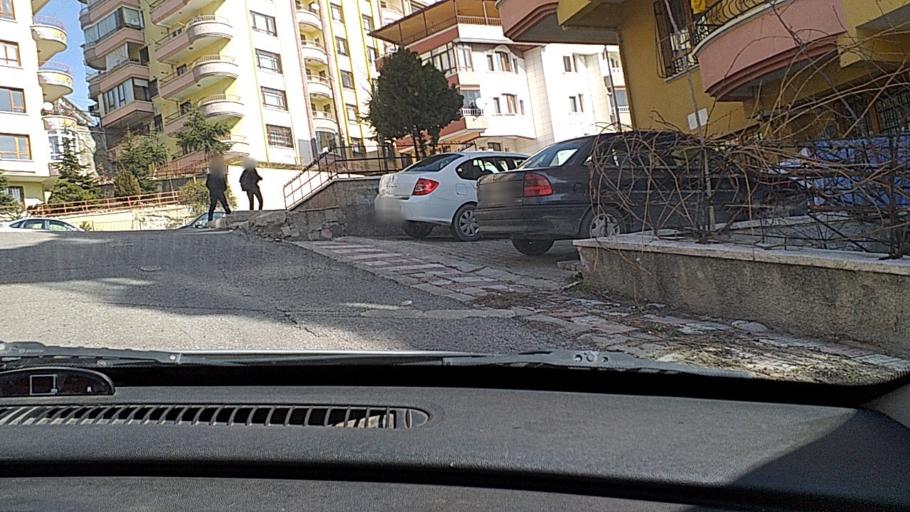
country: TR
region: Ankara
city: Ankara
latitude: 39.9890
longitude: 32.8180
